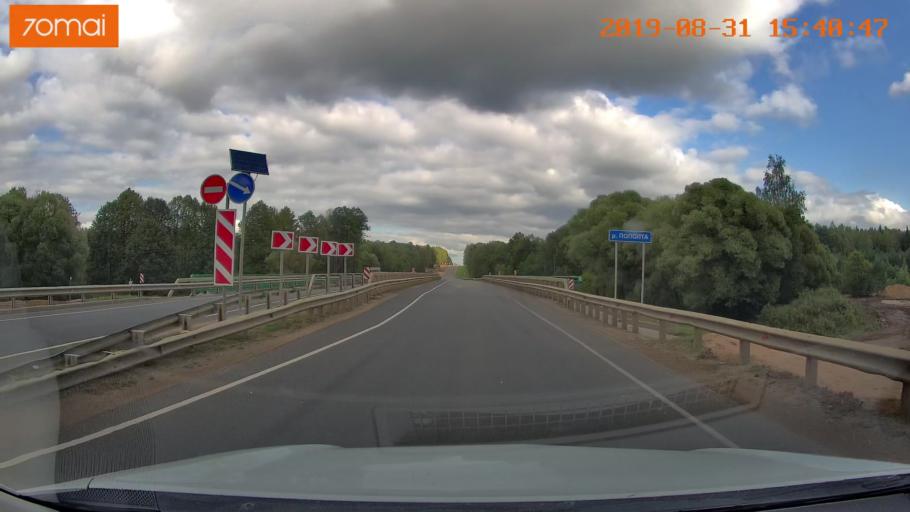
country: RU
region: Kaluga
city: Mosal'sk
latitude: 54.6347
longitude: 34.8446
